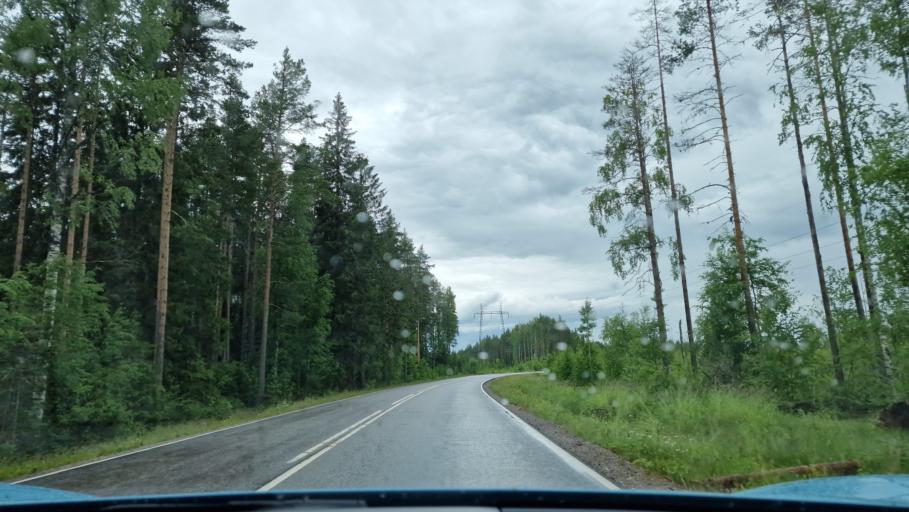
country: FI
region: Central Finland
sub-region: Saarijaervi-Viitasaari
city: Pylkoenmaeki
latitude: 62.6466
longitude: 24.5736
